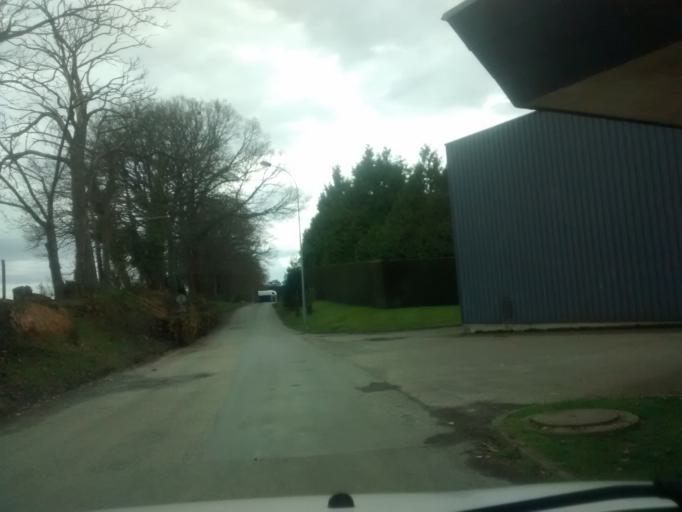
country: FR
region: Brittany
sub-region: Departement d'Ille-et-Vilaine
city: Fouillard
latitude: 48.1770
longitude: -1.6009
